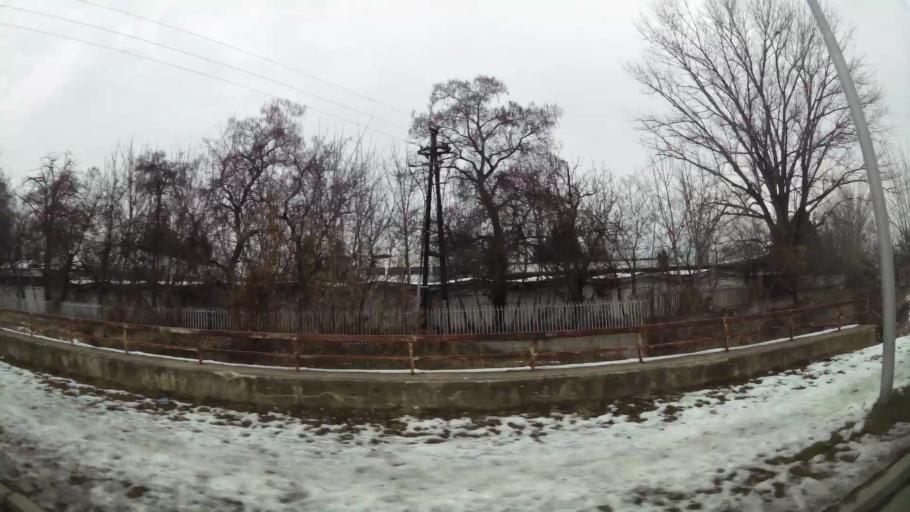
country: MK
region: Butel
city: Butel
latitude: 42.0287
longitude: 21.4355
